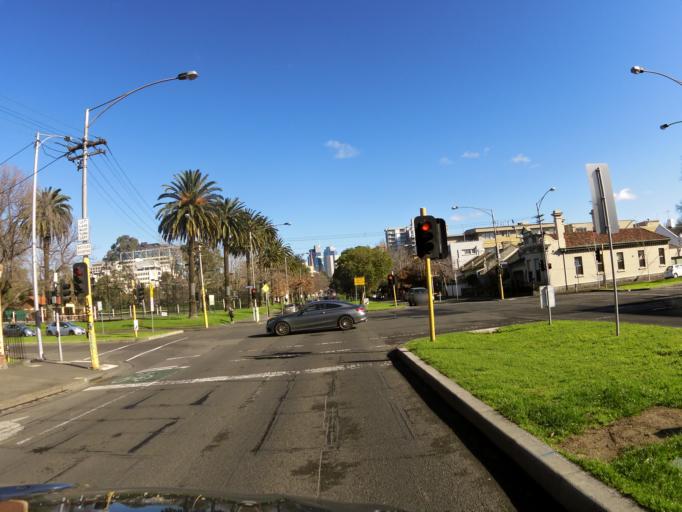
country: AU
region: Victoria
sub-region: Melbourne
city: East Melbourne
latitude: -37.8111
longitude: 144.9891
